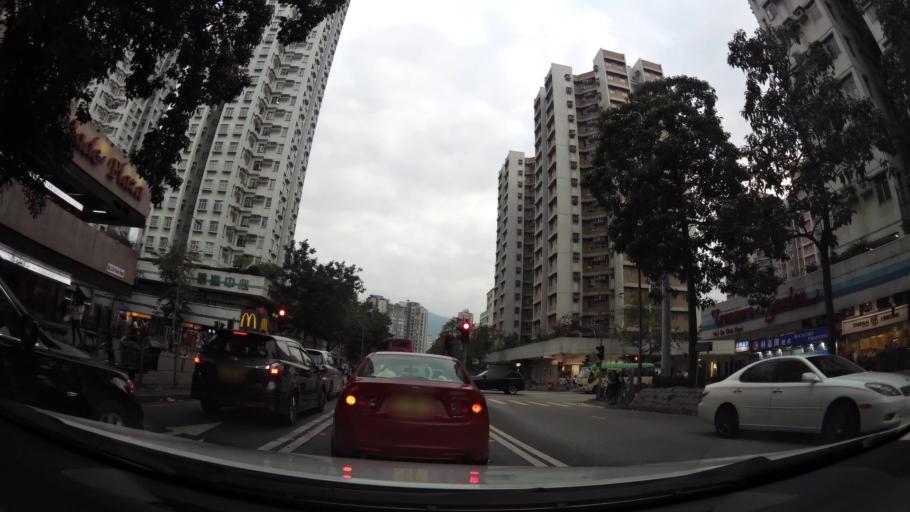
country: HK
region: Tai Po
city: Tai Po
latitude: 22.4532
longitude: 114.1674
